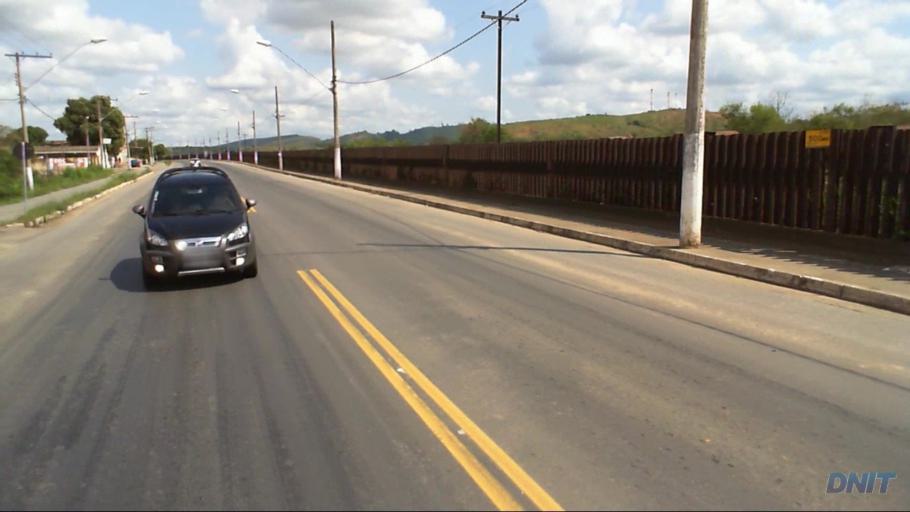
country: BR
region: Minas Gerais
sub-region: Governador Valadares
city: Governador Valadares
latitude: -18.8910
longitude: -41.9756
